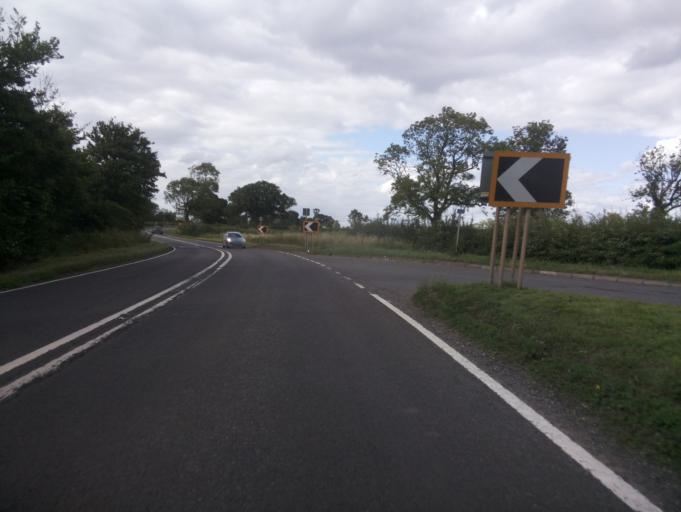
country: GB
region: England
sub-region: Warwickshire
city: Hartshill
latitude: 52.5742
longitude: -1.4790
